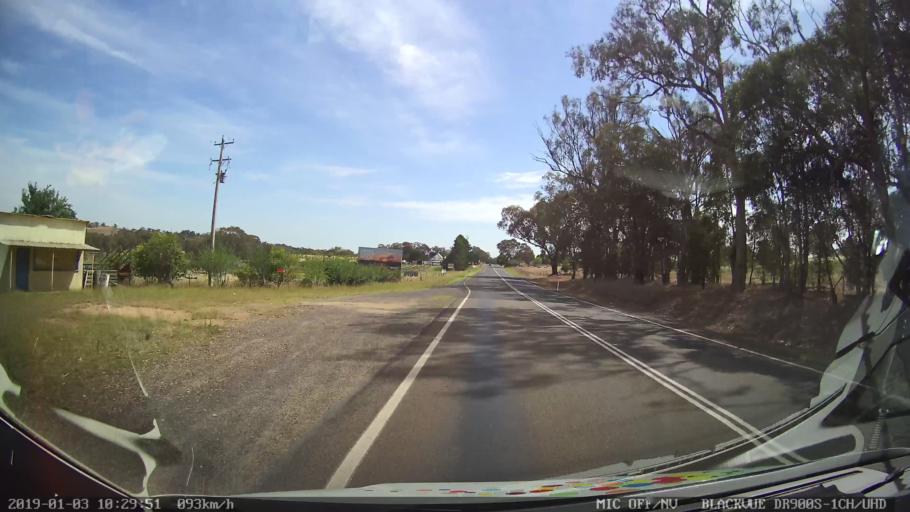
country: AU
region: New South Wales
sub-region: Young
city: Young
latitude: -34.3687
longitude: 148.2621
